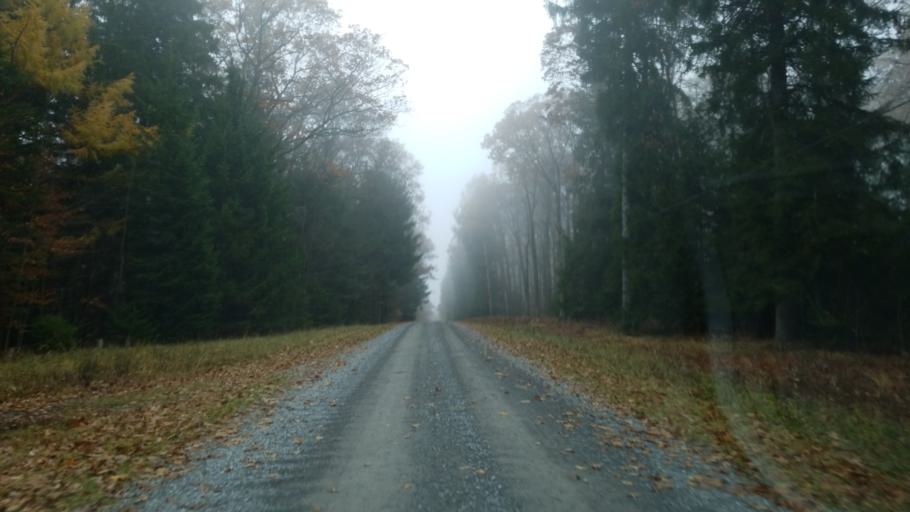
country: US
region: Pennsylvania
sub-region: Clearfield County
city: Clearfield
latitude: 41.1029
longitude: -78.5265
